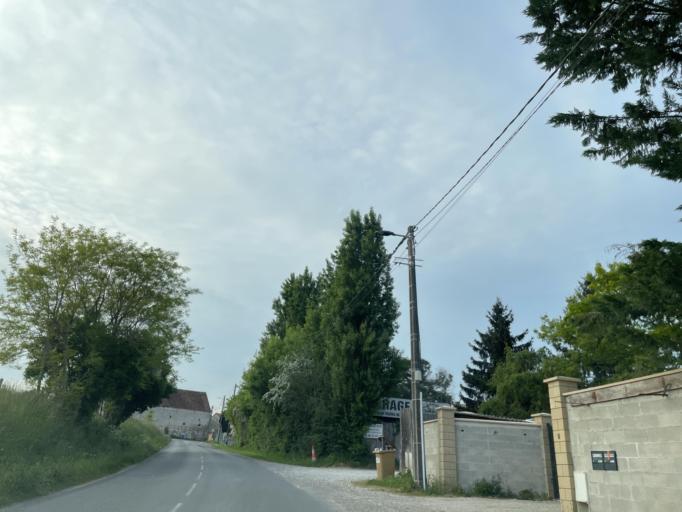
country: FR
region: Ile-de-France
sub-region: Departement de Seine-et-Marne
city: Bouleurs
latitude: 48.9057
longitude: 2.9134
